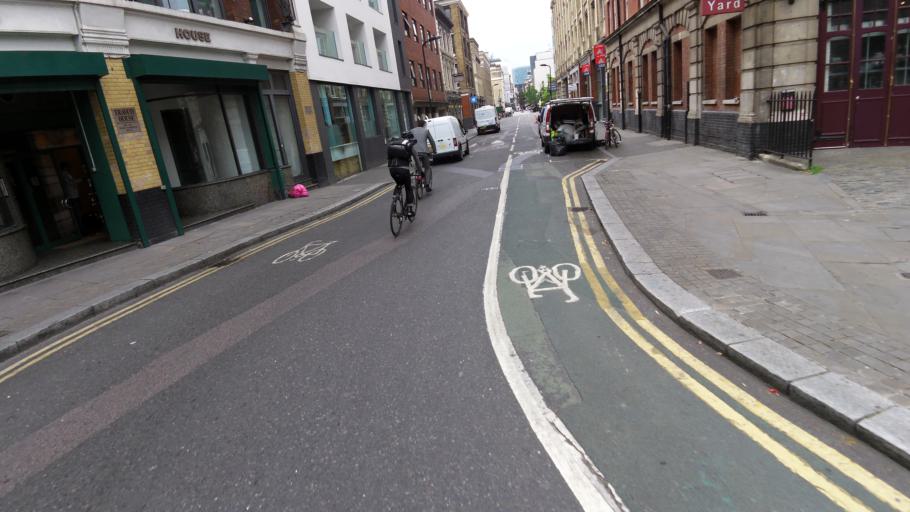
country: GB
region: England
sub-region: Greater London
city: Barbican
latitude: 51.5259
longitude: -0.0838
